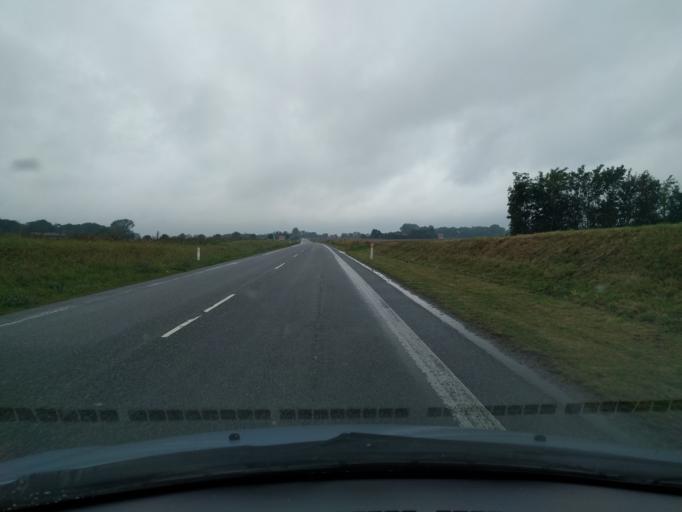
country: DK
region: Zealand
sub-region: Guldborgsund Kommune
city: Stubbekobing
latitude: 54.8910
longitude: 12.0143
